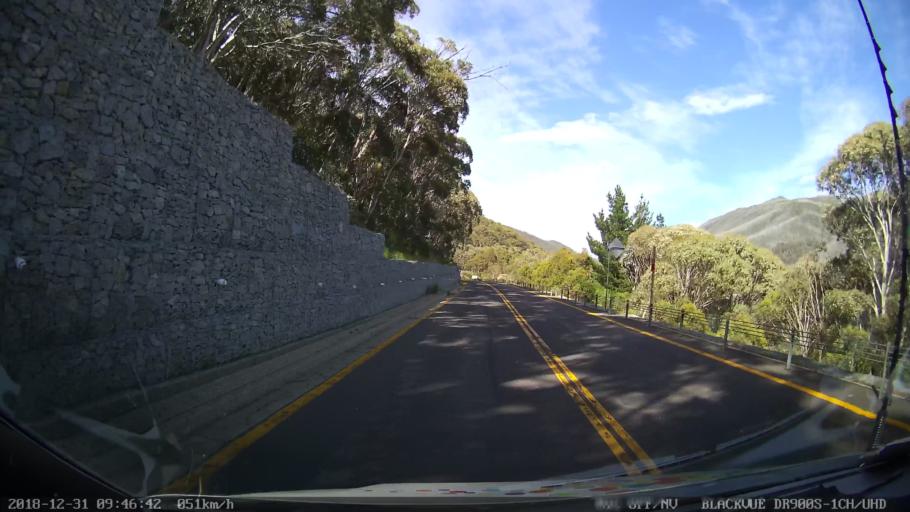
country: AU
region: New South Wales
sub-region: Snowy River
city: Jindabyne
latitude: -36.5051
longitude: 148.3073
